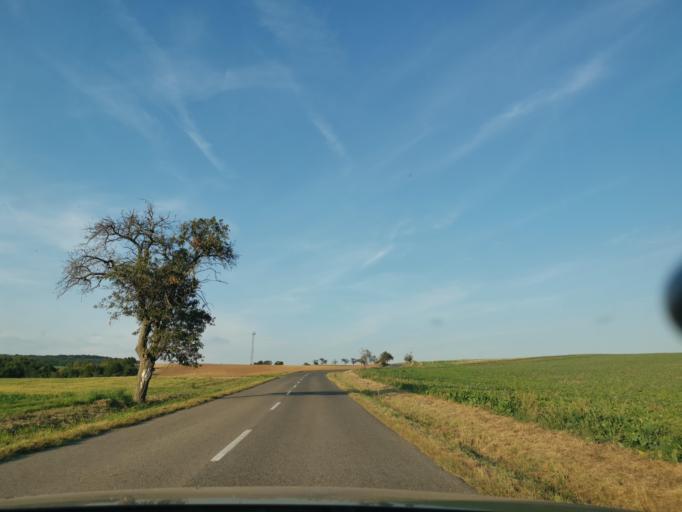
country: SK
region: Trnavsky
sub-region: Okres Senica
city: Senica
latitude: 48.7140
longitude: 17.2884
